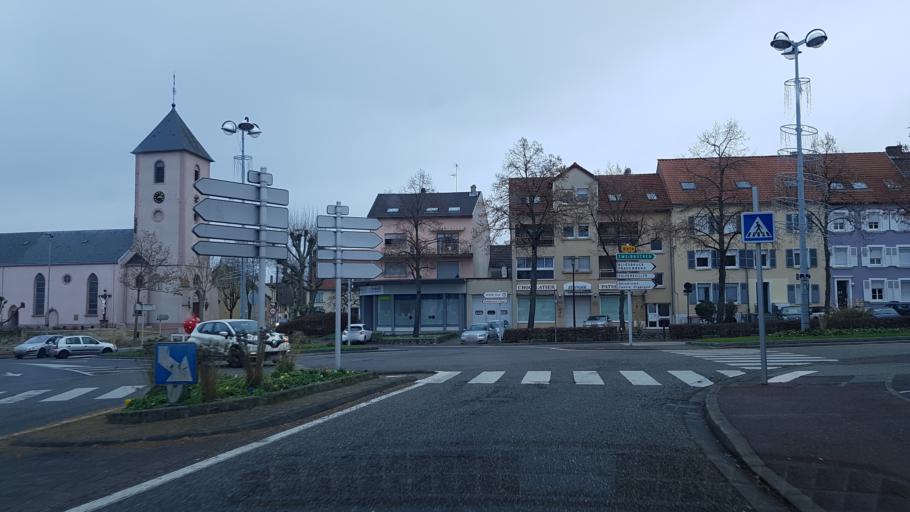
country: FR
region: Lorraine
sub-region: Departement de la Moselle
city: Sarreguemines
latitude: 49.1197
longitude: 7.0901
